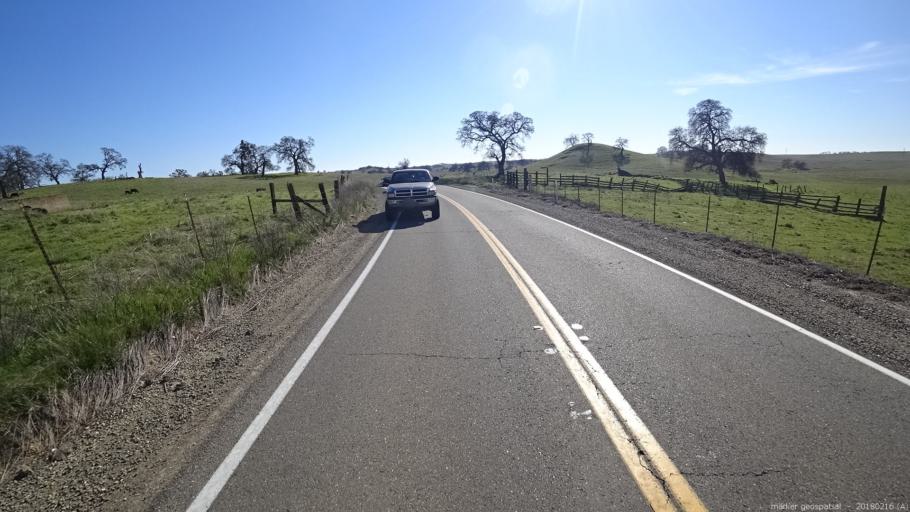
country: US
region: California
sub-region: Sacramento County
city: Rancho Murieta
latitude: 38.5885
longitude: -121.1303
